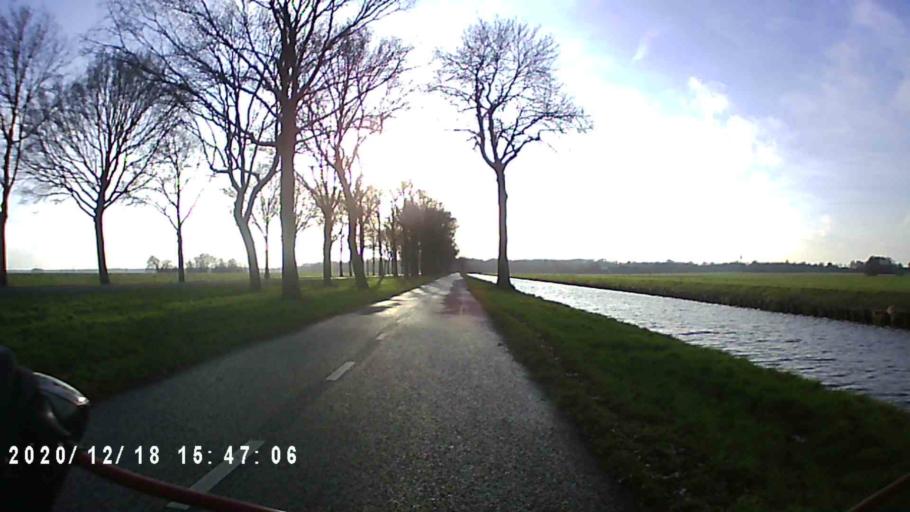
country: NL
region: Drenthe
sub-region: Gemeente Tynaarlo
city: Zuidlaren
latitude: 53.1049
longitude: 6.7036
